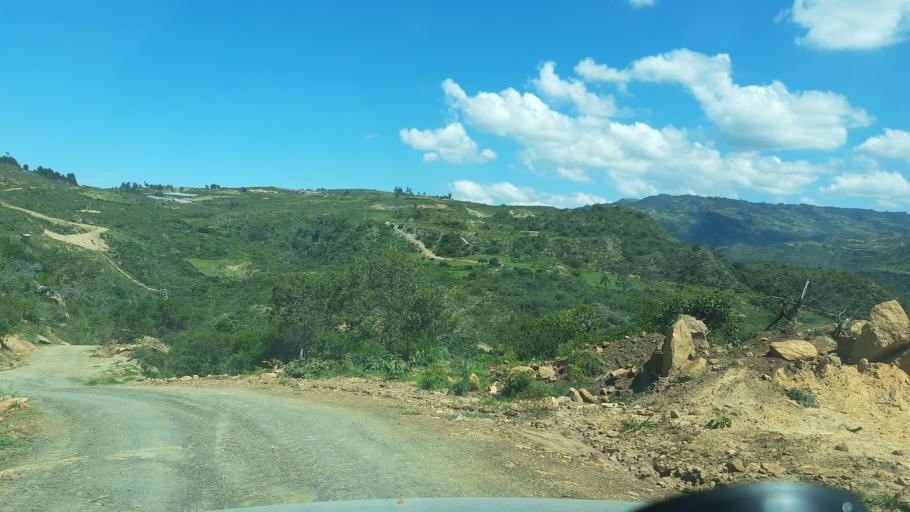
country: CO
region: Boyaca
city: Santa Sofia
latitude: 5.6946
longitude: -73.5830
